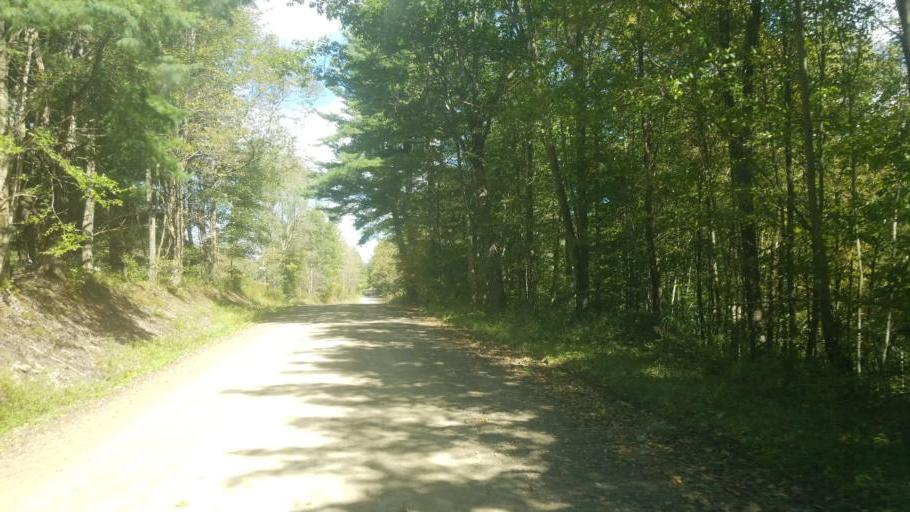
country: US
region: New York
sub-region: Allegany County
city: Cuba
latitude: 42.1769
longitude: -78.3316
